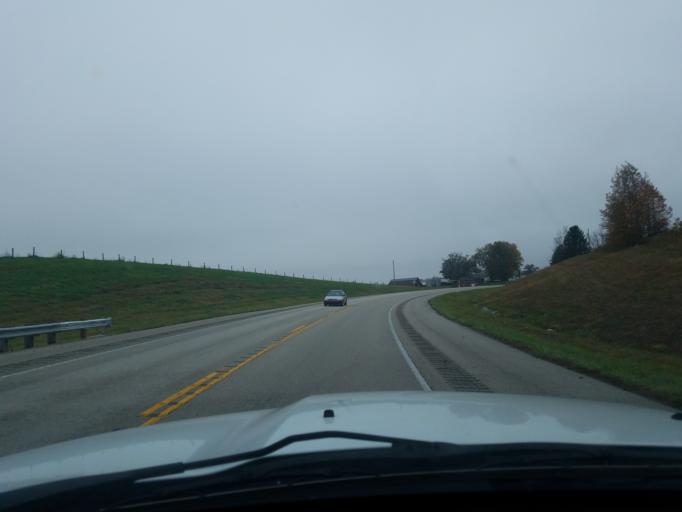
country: US
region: Kentucky
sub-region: Green County
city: Greensburg
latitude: 37.4181
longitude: -85.5119
